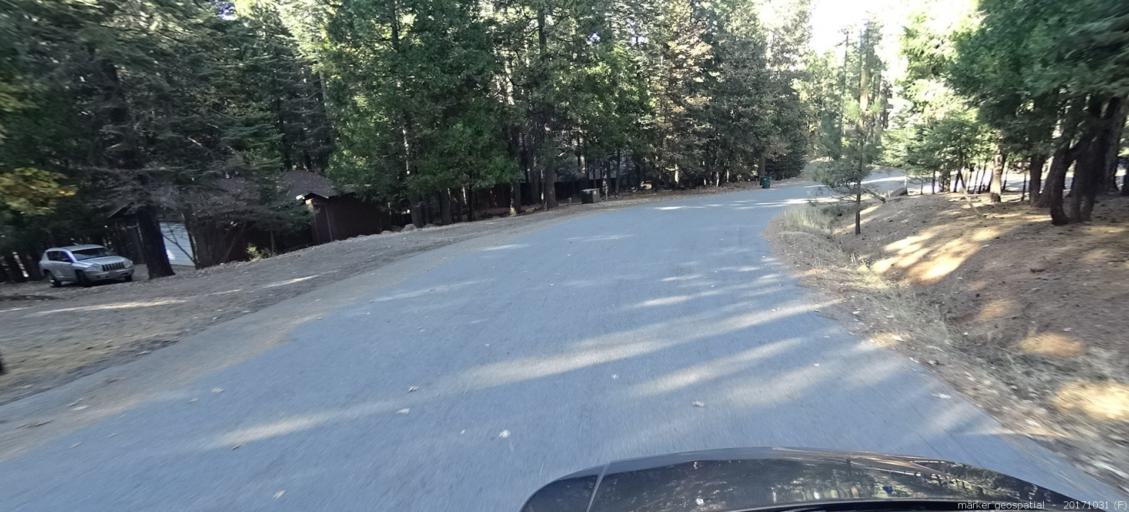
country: US
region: California
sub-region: Shasta County
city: Shingletown
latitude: 40.5014
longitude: -121.9020
